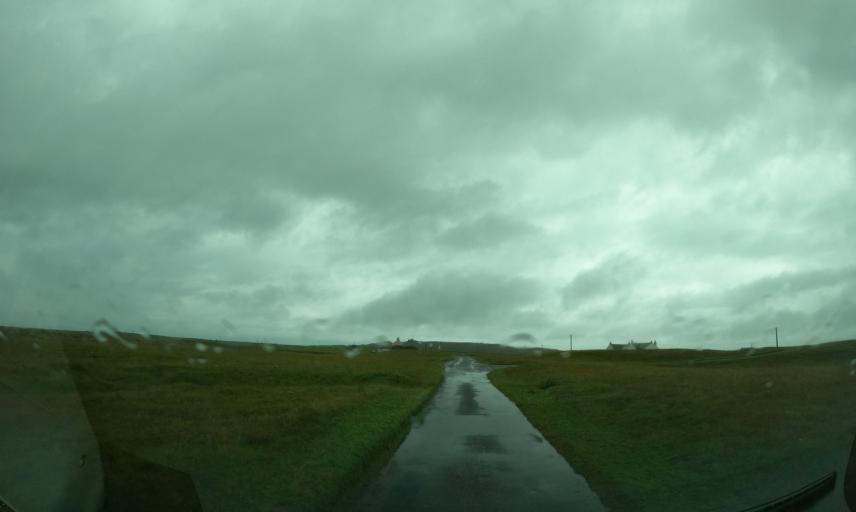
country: GB
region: Scotland
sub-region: Eilean Siar
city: Barra
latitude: 56.5154
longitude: -6.8154
